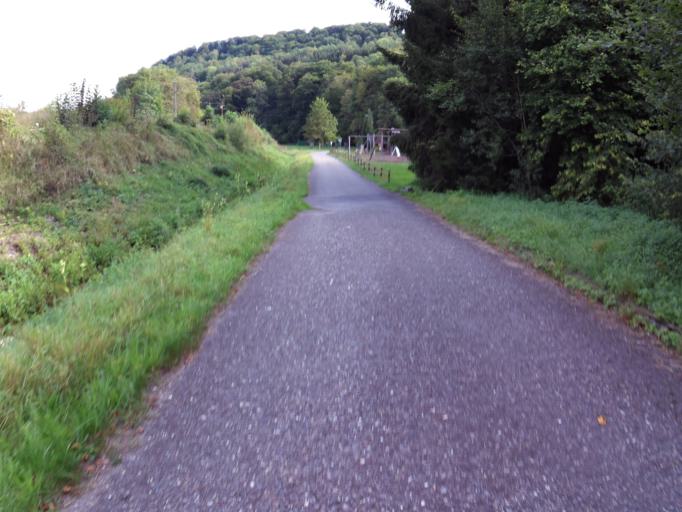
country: DE
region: Baden-Wuerttemberg
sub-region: Freiburg Region
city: Villingendorf
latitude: 48.2211
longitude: 8.5990
